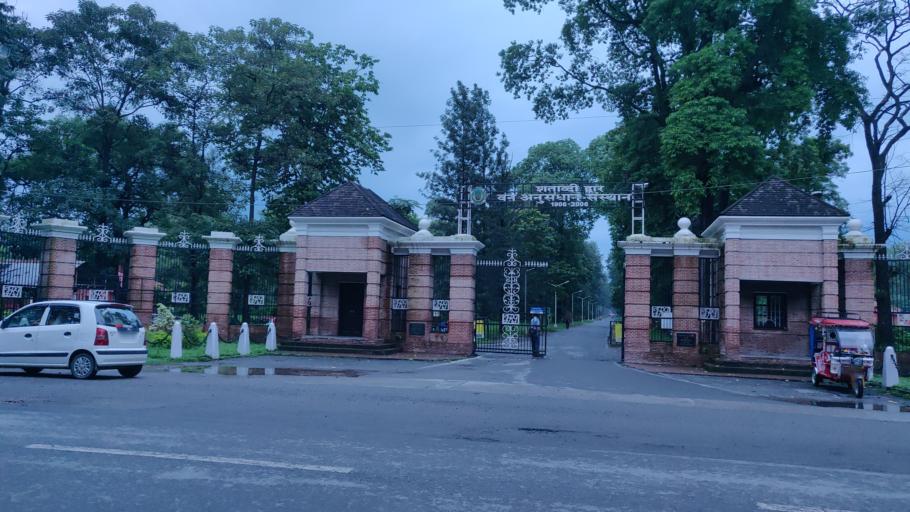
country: IN
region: Uttarakhand
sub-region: Dehradun
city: Dehradun
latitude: 30.3326
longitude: 77.9955
